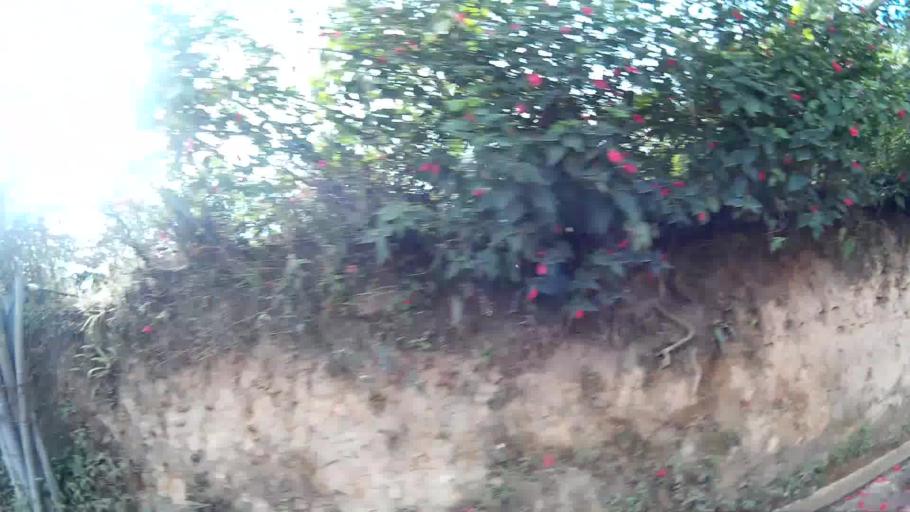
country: CO
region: Valle del Cauca
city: Ulloa
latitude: 4.7328
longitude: -75.7170
